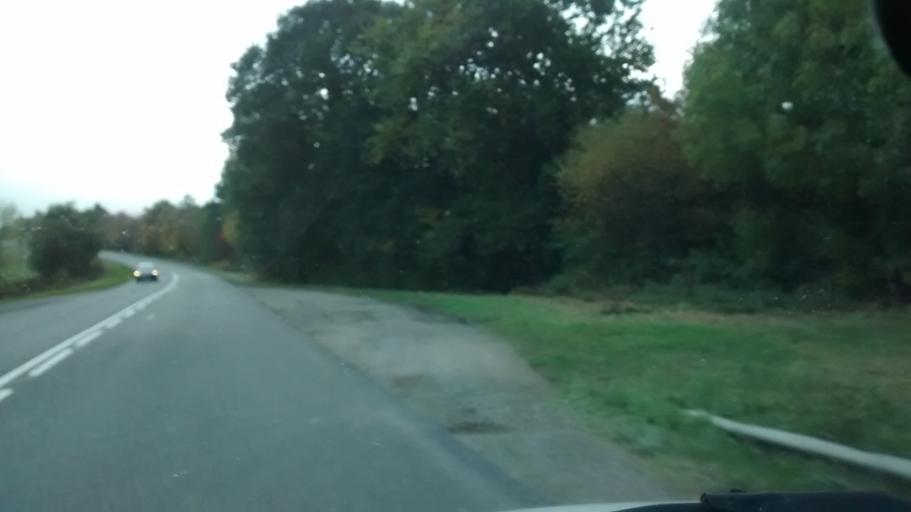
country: FR
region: Brittany
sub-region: Departement d'Ille-et-Vilaine
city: Acigne
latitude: 48.1591
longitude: -1.5166
